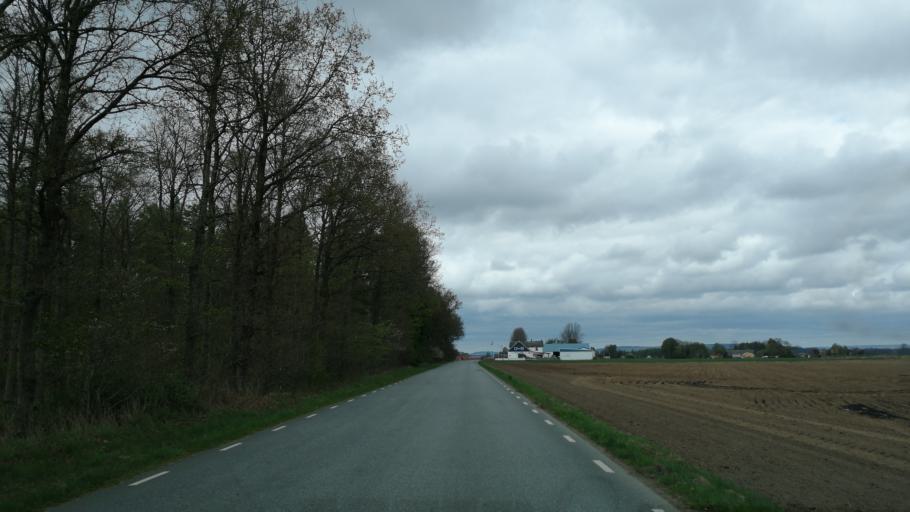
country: SE
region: Skane
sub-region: Kristianstads Kommun
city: Fjalkinge
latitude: 56.0546
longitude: 14.3332
